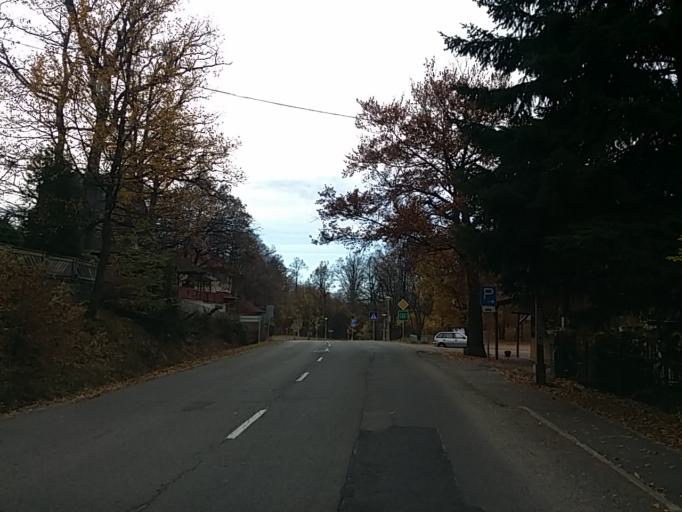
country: HU
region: Heves
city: Paradsasvar
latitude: 47.8694
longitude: 19.9785
